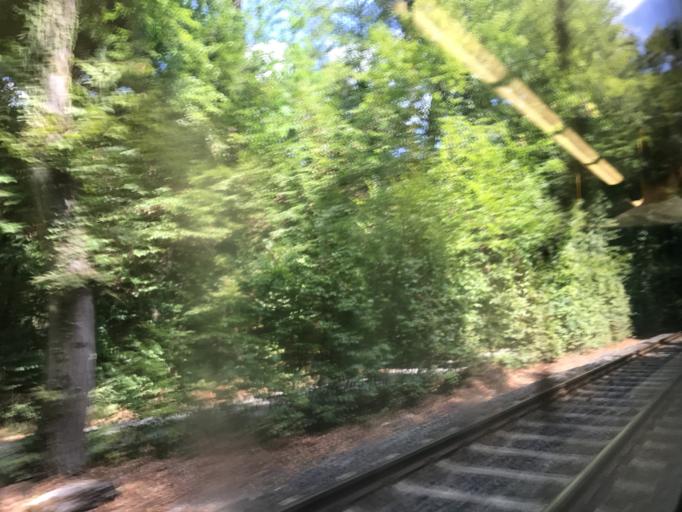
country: DE
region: Hesse
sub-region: Regierungsbezirk Darmstadt
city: Neu Isenburg
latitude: 50.0713
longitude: 8.6769
